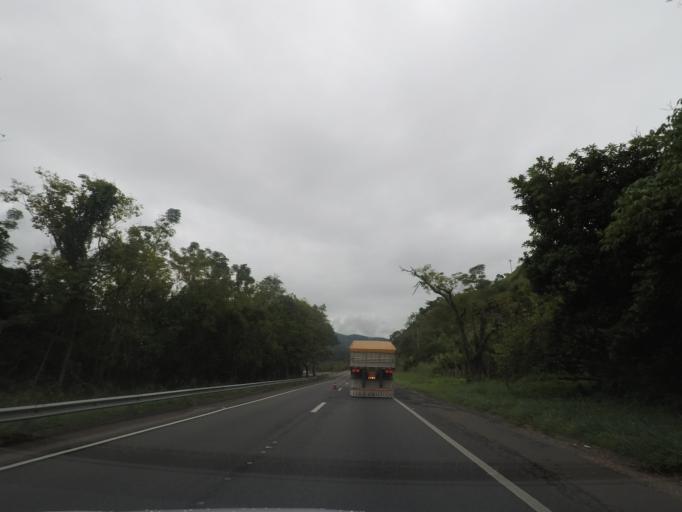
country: BR
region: Sao Paulo
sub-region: Cajati
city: Cajati
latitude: -24.8129
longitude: -48.2093
